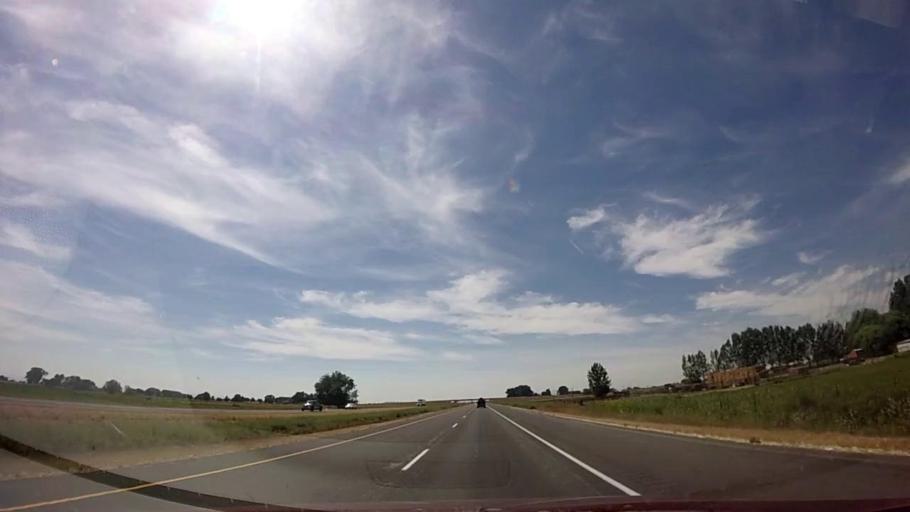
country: US
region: Idaho
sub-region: Minidoka County
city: Rupert
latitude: 42.5690
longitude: -113.6964
